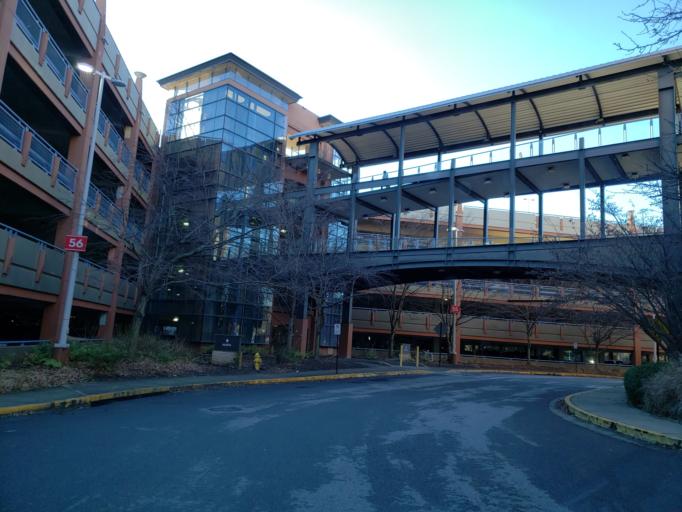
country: US
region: Georgia
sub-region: DeKalb County
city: Dunwoody
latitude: 33.9228
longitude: -84.3423
